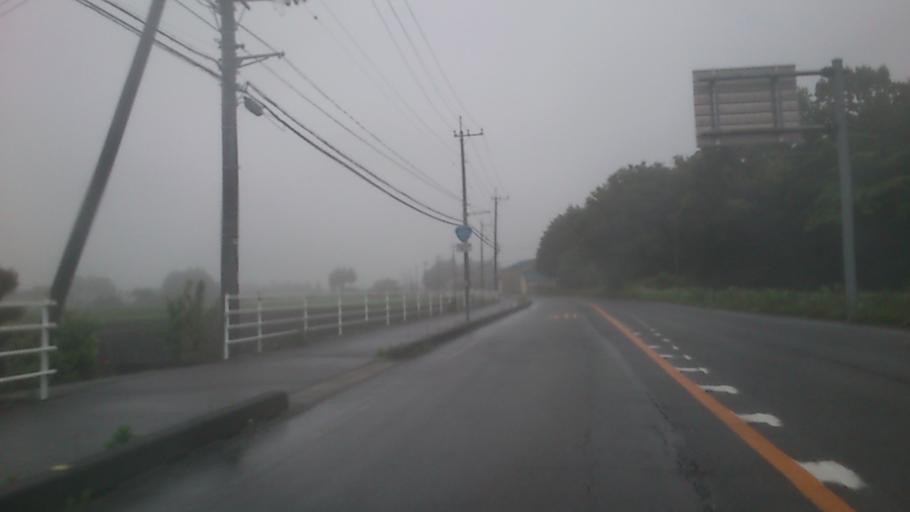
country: JP
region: Tochigi
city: Otawara
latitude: 36.8389
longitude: 140.0648
